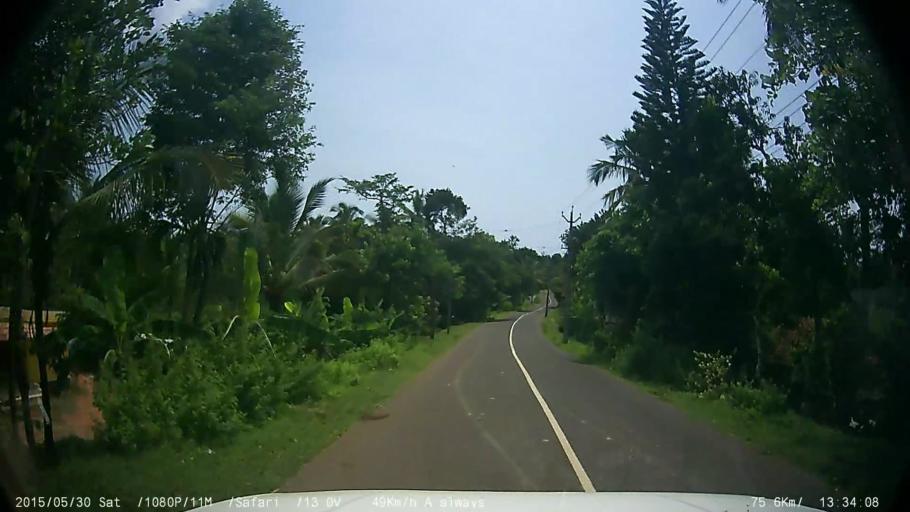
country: IN
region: Kerala
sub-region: Wayanad
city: Panamaram
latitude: 11.8232
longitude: 76.0673
